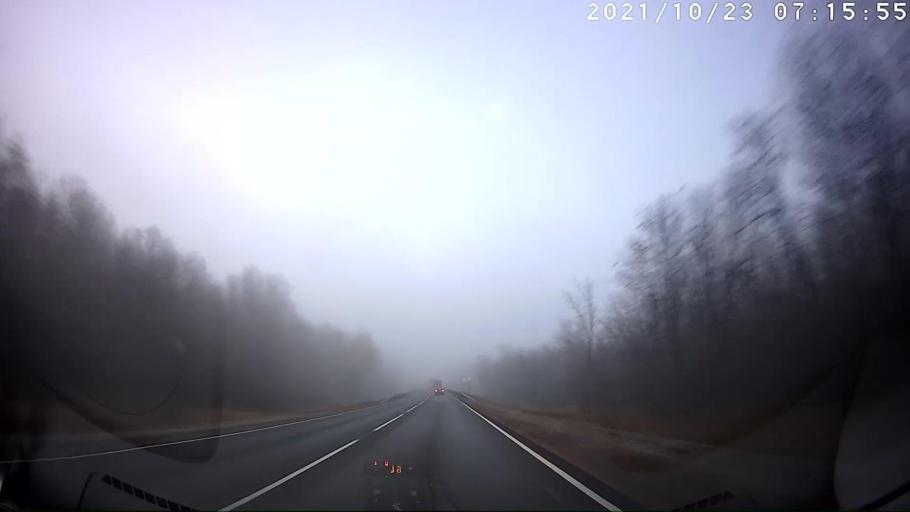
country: RU
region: Saratov
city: Khvalynsk
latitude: 52.4826
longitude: 48.0132
